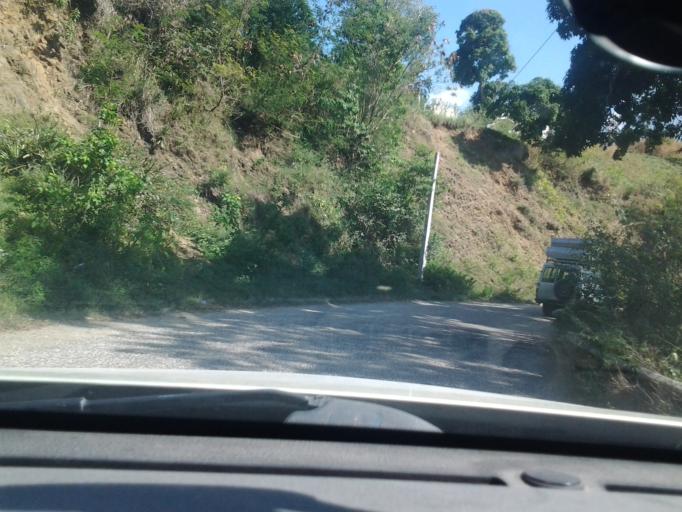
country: HT
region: Ouest
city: Leogane
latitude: 18.3971
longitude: -72.6331
